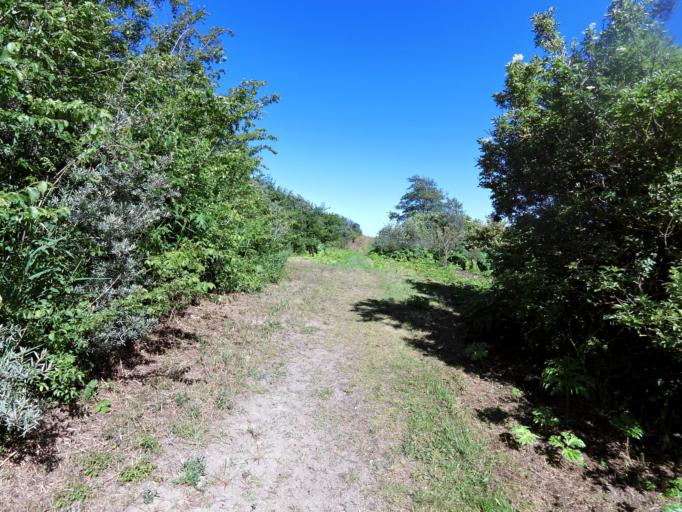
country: NL
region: South Holland
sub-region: Gemeente Goeree-Overflakkee
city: Goedereede
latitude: 51.8128
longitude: 4.0401
